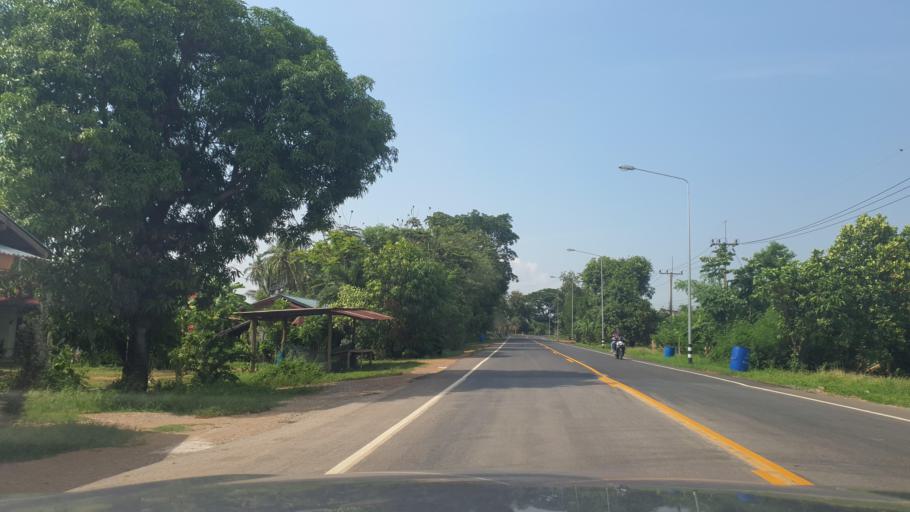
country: TH
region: Sukhothai
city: Si Samrong
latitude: 17.1654
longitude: 99.8318
